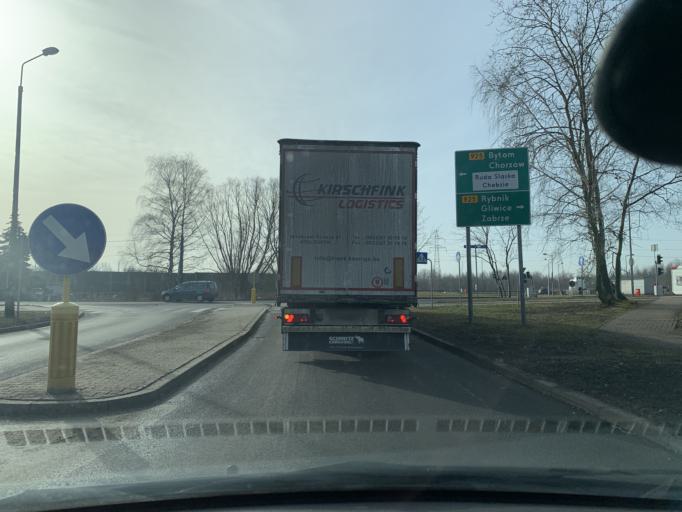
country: PL
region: Silesian Voivodeship
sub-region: Ruda Slaska
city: Ruda Slaska
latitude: 50.3013
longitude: 18.8683
